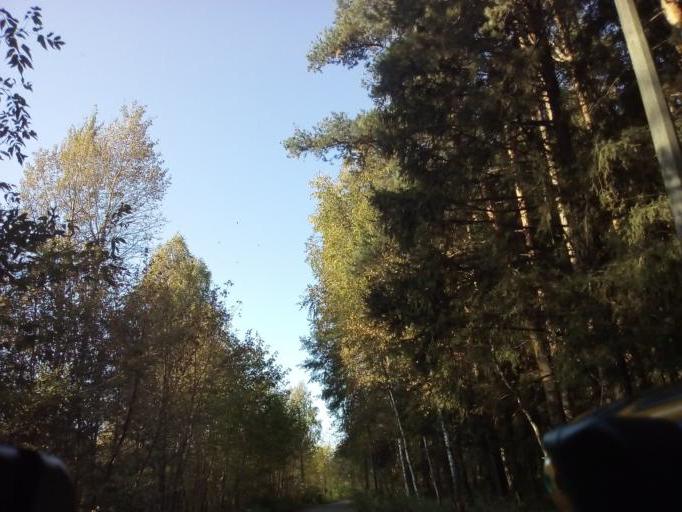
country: RU
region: Moskovskaya
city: Gzhel'
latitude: 55.5966
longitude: 38.3202
